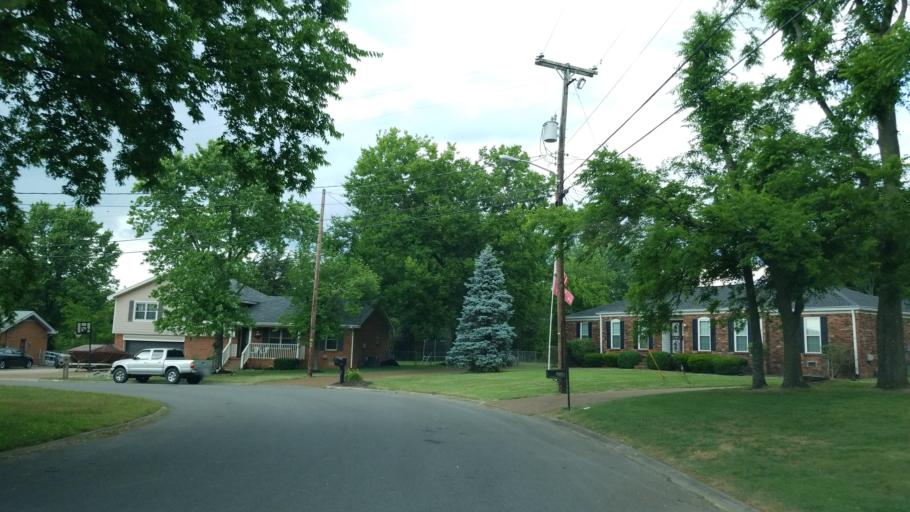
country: US
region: Tennessee
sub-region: Rutherford County
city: La Vergne
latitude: 36.0957
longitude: -86.6079
